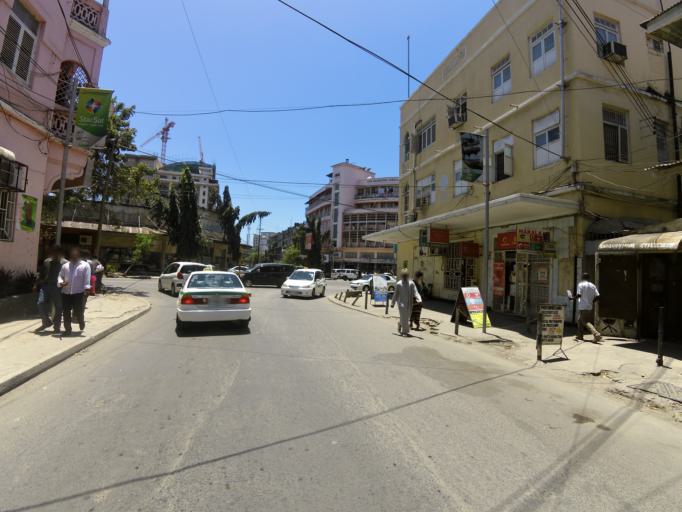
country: TZ
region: Dar es Salaam
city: Dar es Salaam
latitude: -6.8162
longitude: 39.2864
